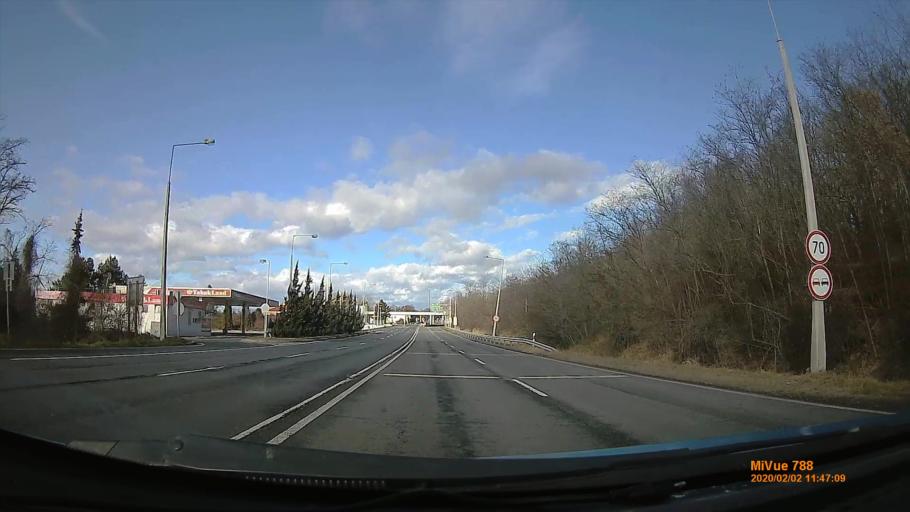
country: AT
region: Burgenland
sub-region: Eisenstadt-Umgebung
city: Klingenbach
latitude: 47.7378
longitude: 16.5484
